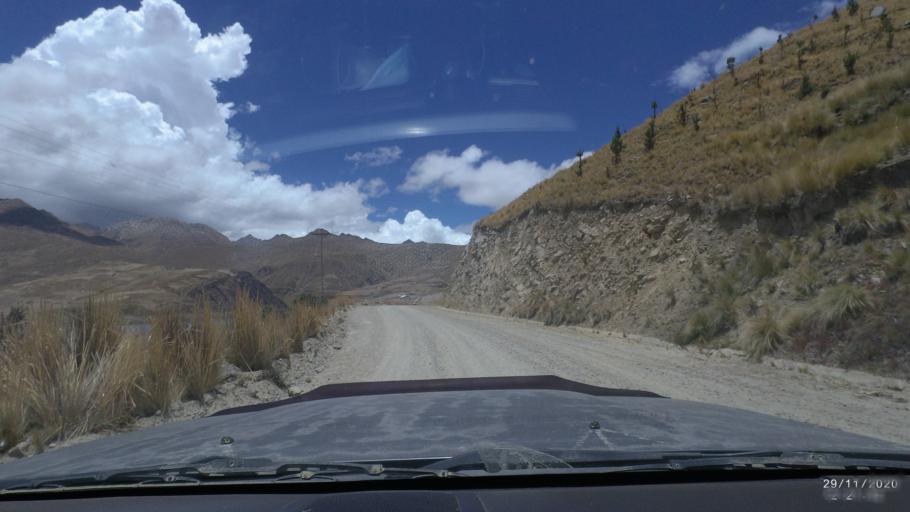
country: BO
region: Cochabamba
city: Cochabamba
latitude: -17.0983
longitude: -66.3245
